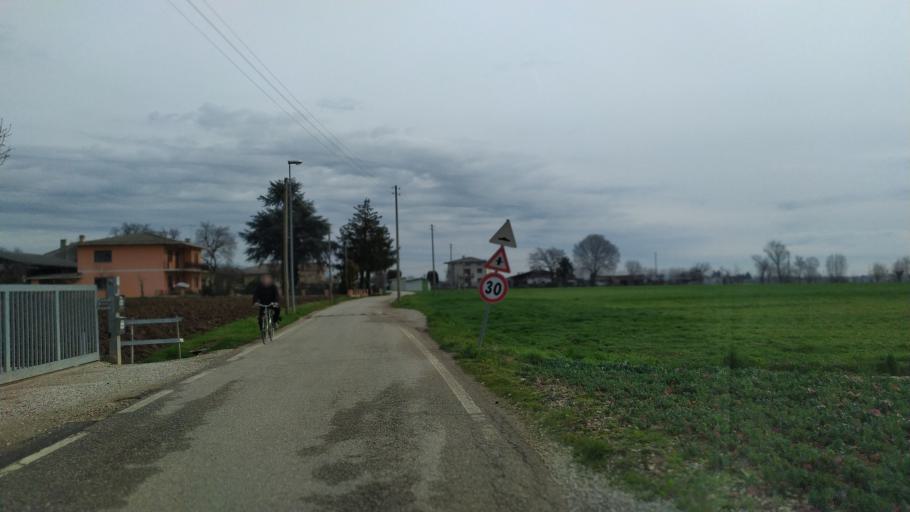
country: IT
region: Veneto
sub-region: Provincia di Vicenza
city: Isola Vicentina
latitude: 45.6534
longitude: 11.4625
